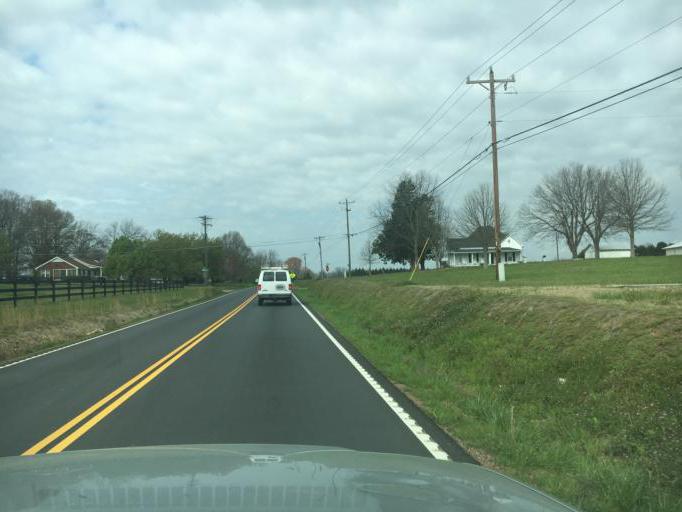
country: US
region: South Carolina
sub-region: Spartanburg County
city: Inman Mills
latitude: 35.0585
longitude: -82.1527
